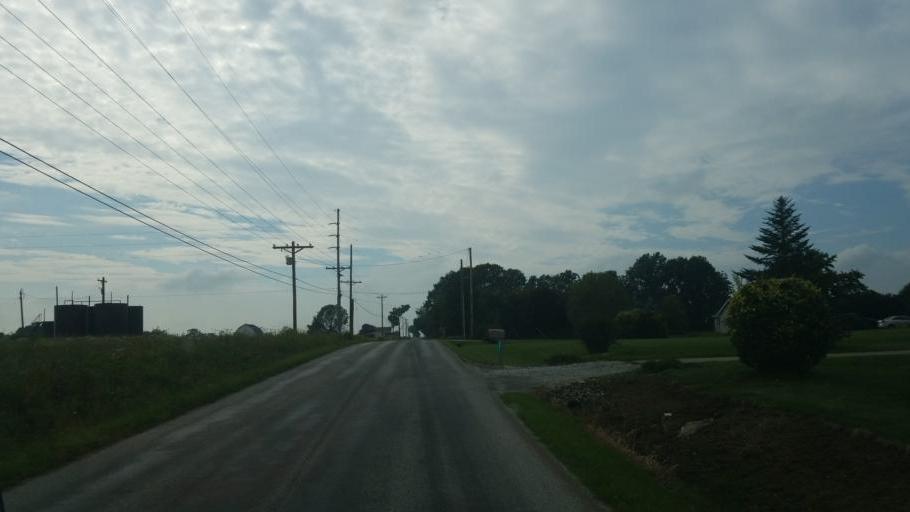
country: US
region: Ohio
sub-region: Wayne County
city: Wooster
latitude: 40.9011
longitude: -81.9811
